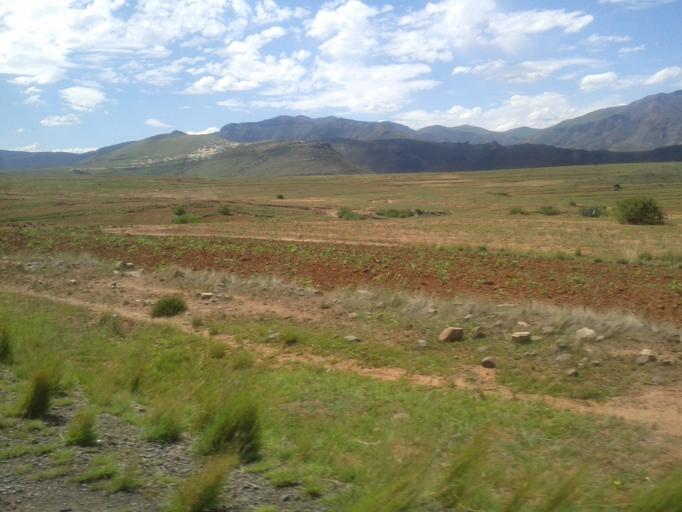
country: LS
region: Qacha's Nek
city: Qacha's Nek
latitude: -30.0373
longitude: 28.3356
